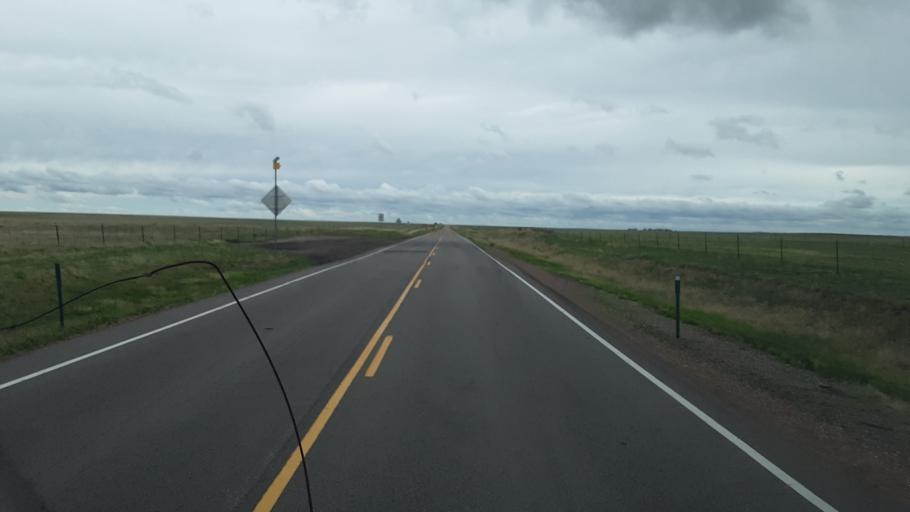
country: US
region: Colorado
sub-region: Lincoln County
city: Hugo
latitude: 38.8520
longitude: -103.7025
